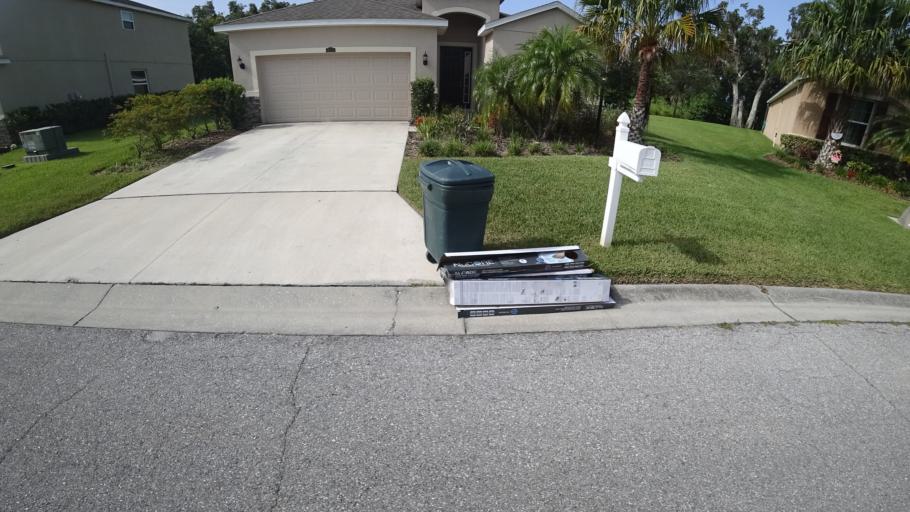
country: US
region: Florida
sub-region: Manatee County
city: Ellenton
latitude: 27.5501
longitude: -82.5069
